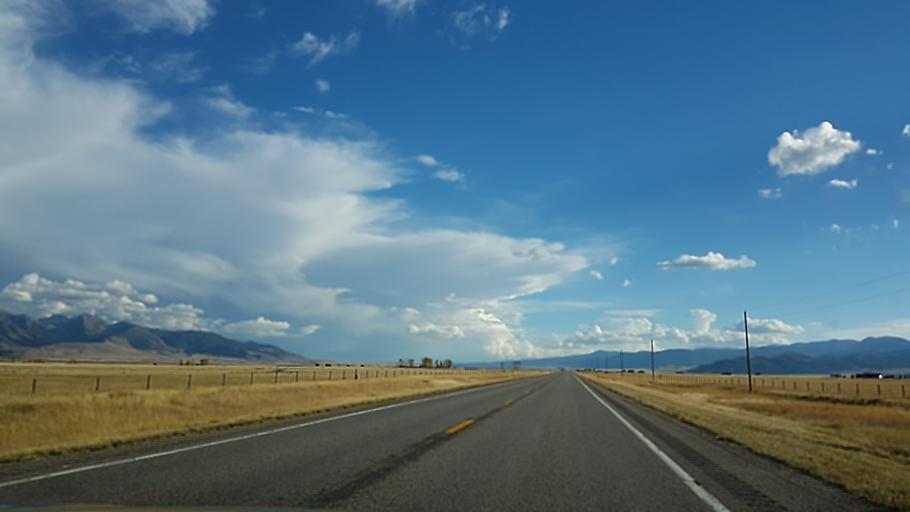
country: US
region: Montana
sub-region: Madison County
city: Virginia City
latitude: 45.1943
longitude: -111.6789
